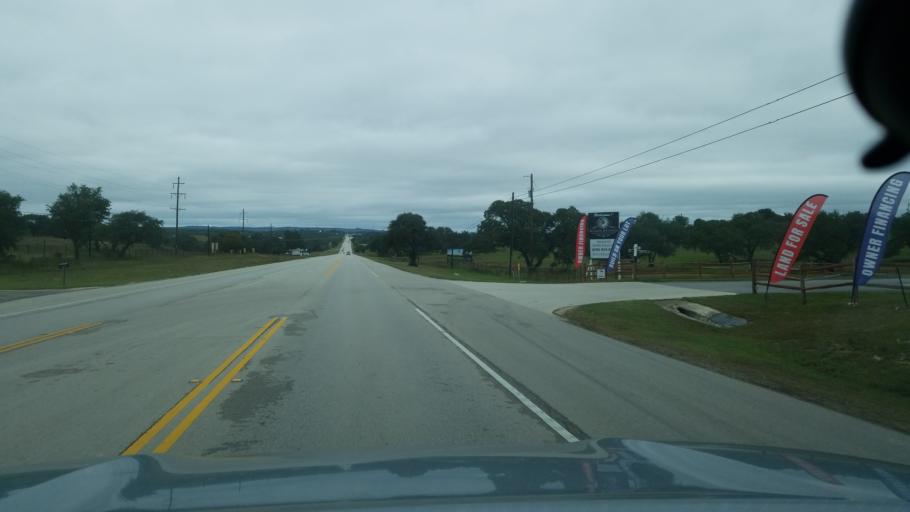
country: US
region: Texas
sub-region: Blanco County
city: Blanco
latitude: 30.0475
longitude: -98.4114
